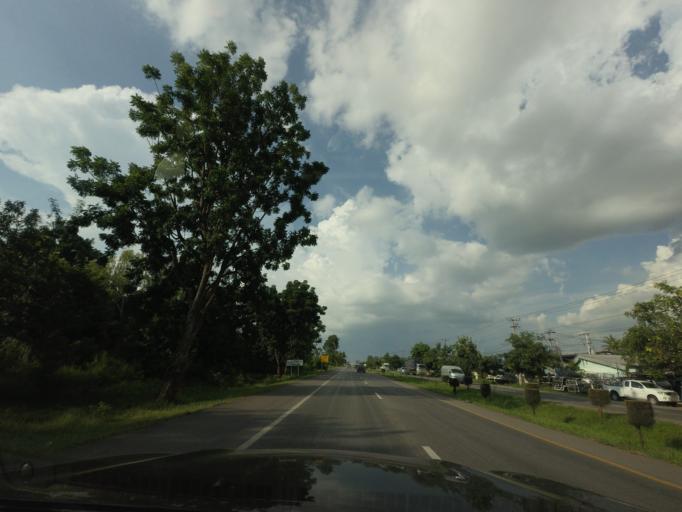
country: TH
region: Khon Kaen
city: Ban Haet
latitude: 16.2447
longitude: 102.7716
